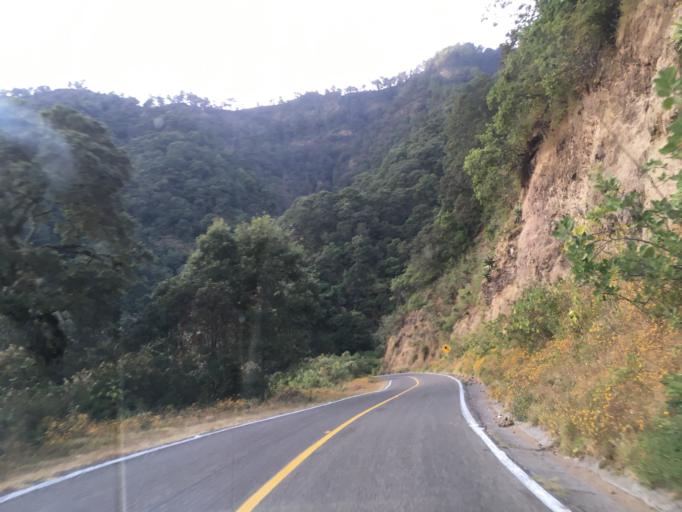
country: MX
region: Michoacan
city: Tzitzio
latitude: 19.6697
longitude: -100.9219
